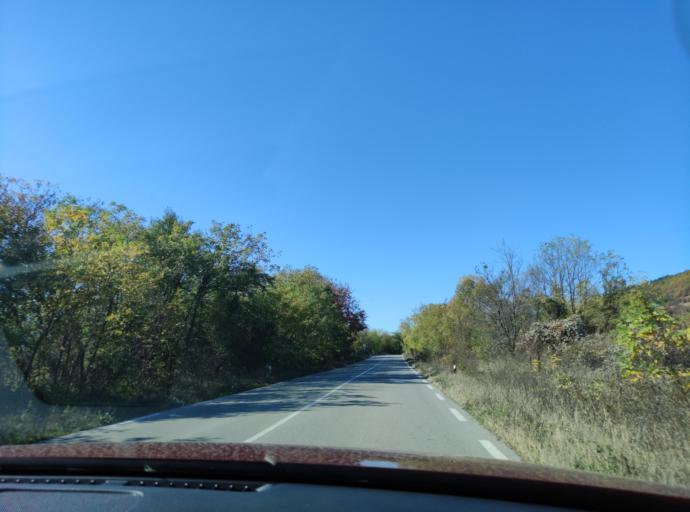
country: BG
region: Montana
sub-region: Obshtina Chiprovtsi
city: Chiprovtsi
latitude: 43.4293
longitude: 22.9972
